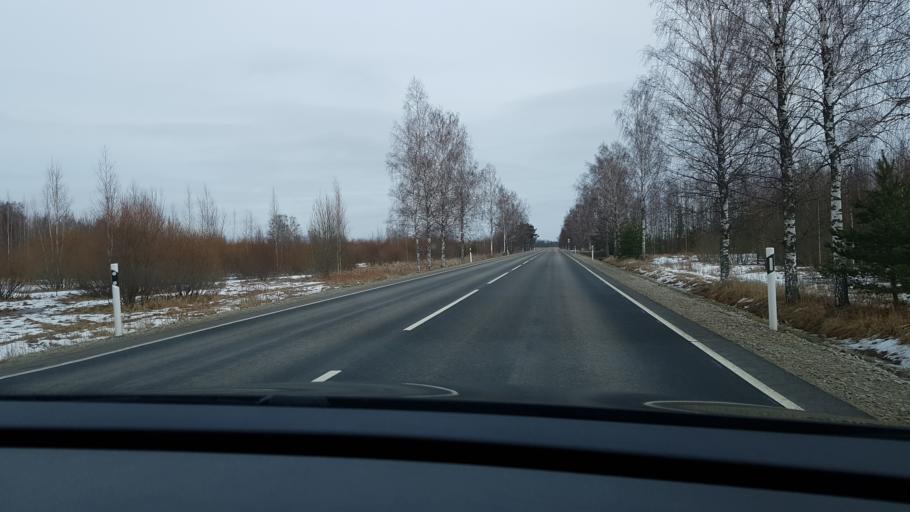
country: EE
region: Paernumaa
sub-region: Sindi linn
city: Sindi
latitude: 58.4128
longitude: 24.6838
